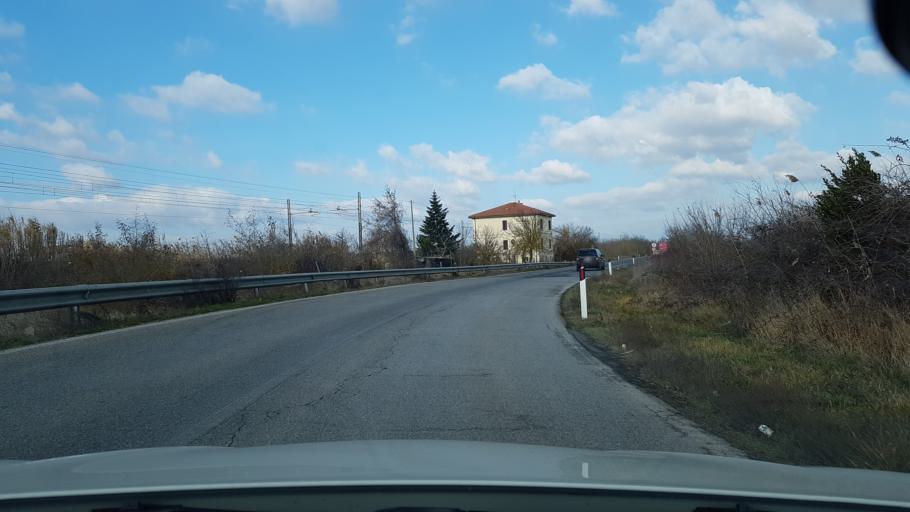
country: IT
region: Umbria
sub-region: Provincia di Perugia
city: Castiglione del Lago
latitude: 43.1318
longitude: 12.0290
